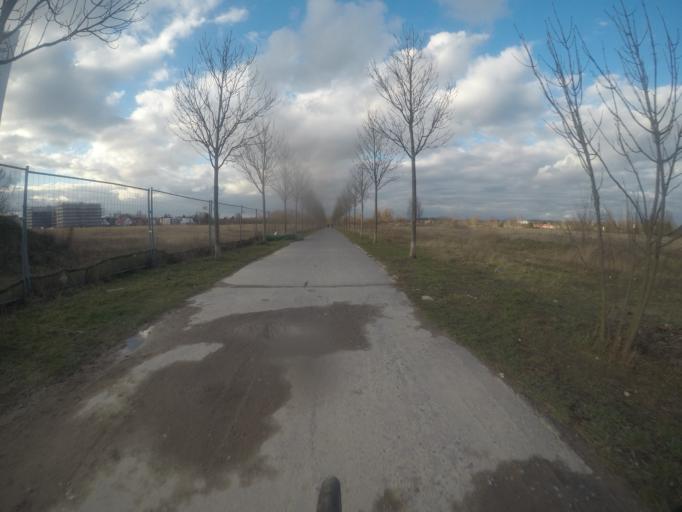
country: DE
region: Brandenburg
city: Ahrensfelde
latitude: 52.5732
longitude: 13.5637
